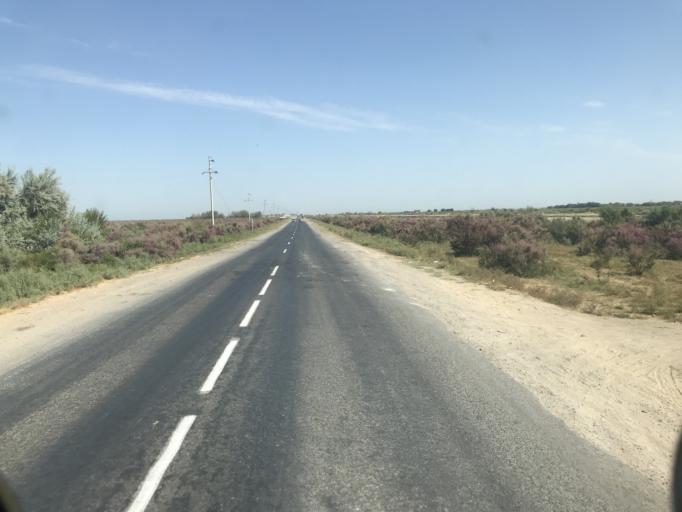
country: KZ
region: Ongtustik Qazaqstan
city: Myrzakent
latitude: 40.6811
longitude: 68.5322
